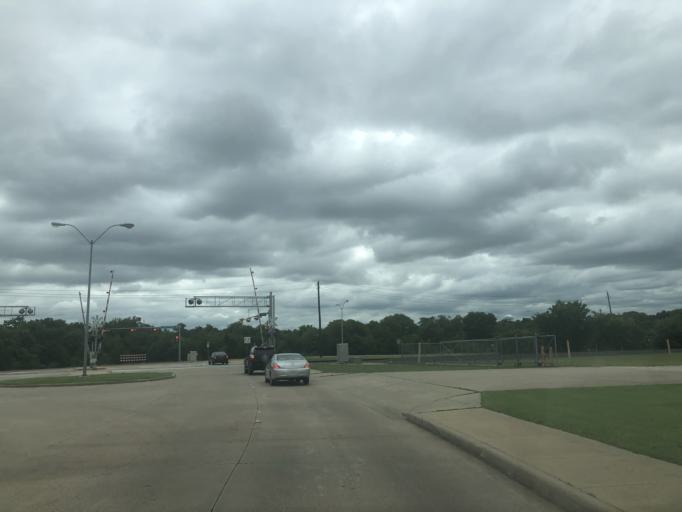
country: US
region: Texas
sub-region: Dallas County
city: Duncanville
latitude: 32.6369
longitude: -96.9239
